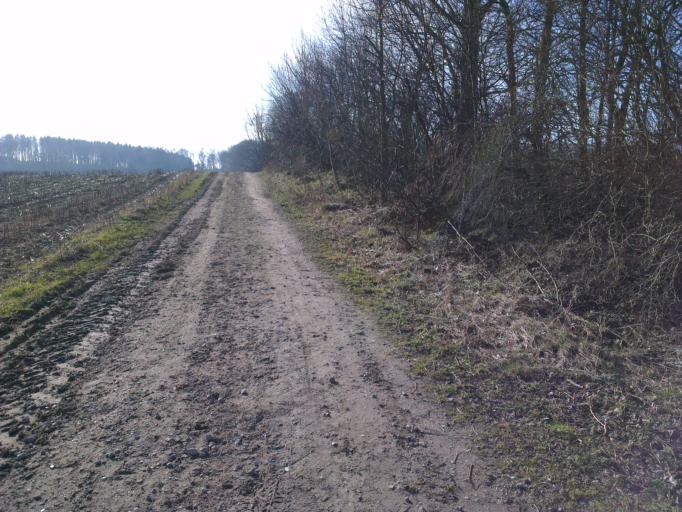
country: DK
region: Capital Region
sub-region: Frederikssund Kommune
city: Skibby
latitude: 55.7875
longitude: 11.9540
